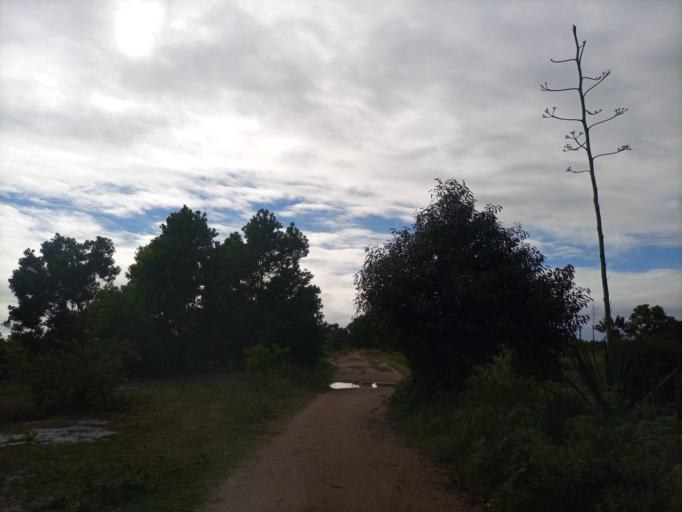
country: MG
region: Anosy
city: Fort Dauphin
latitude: -24.7798
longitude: 47.1807
